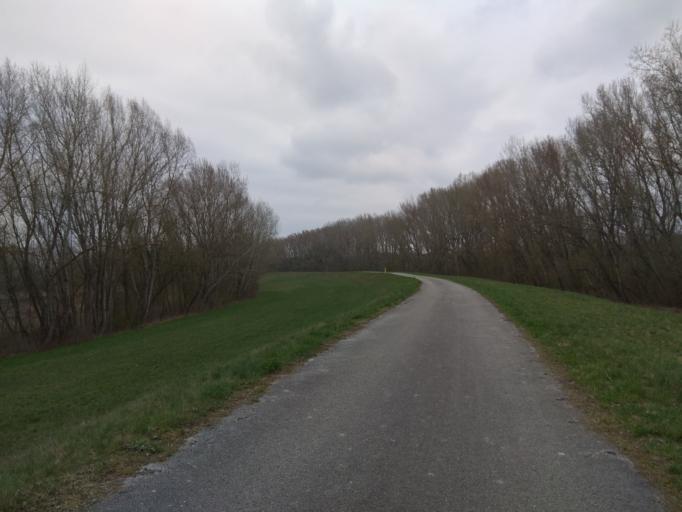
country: HU
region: Gyor-Moson-Sopron
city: Gyor
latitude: 47.7941
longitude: 17.6643
